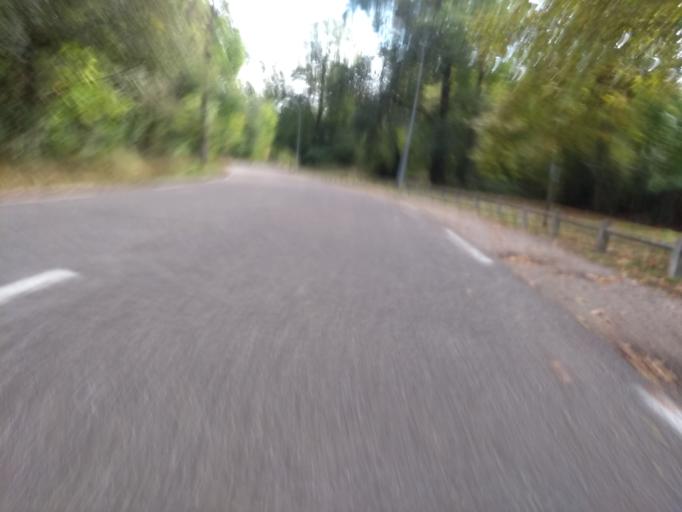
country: FR
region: Aquitaine
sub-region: Departement de la Gironde
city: Canejan
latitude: 44.7698
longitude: -0.6284
